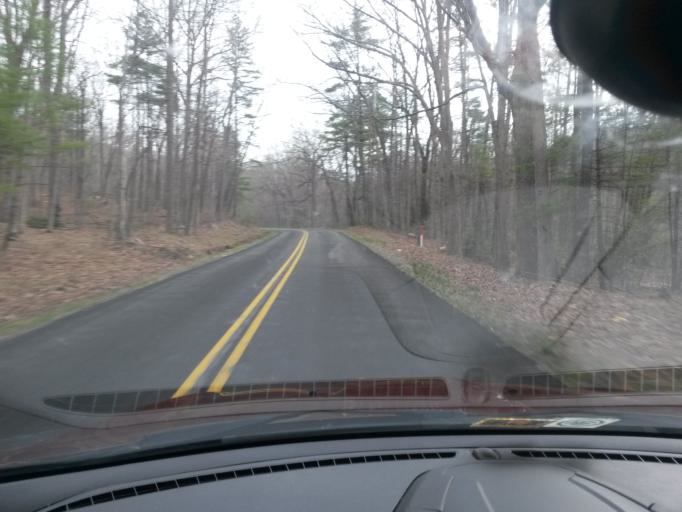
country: US
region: Virginia
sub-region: Alleghany County
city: Clifton Forge
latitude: 37.8334
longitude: -79.6530
